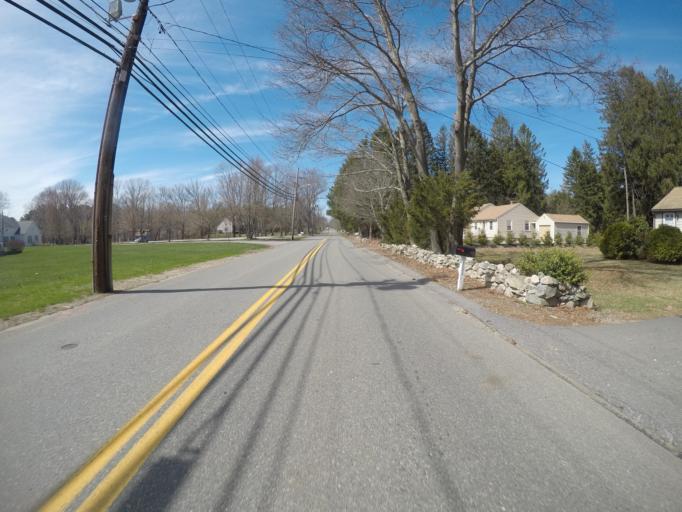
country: US
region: Massachusetts
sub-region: Bristol County
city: Easton
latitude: 42.0258
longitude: -71.0830
